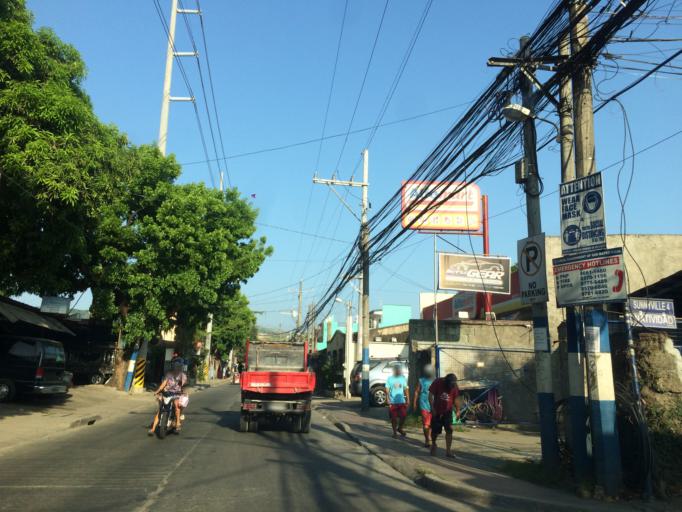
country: PH
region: Calabarzon
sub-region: Province of Rizal
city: San Mateo
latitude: 14.6805
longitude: 121.1209
